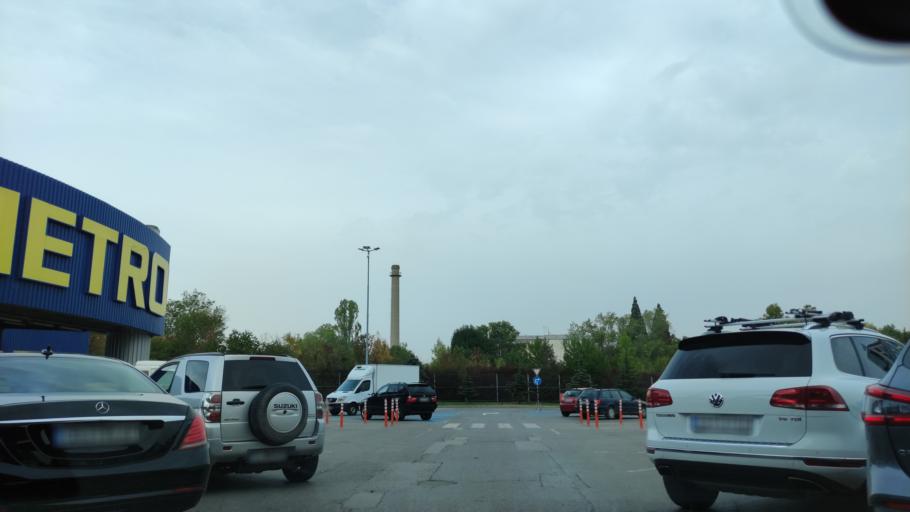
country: BG
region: Sofia-Capital
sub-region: Stolichna Obshtina
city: Sofia
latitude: 42.6473
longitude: 23.3936
